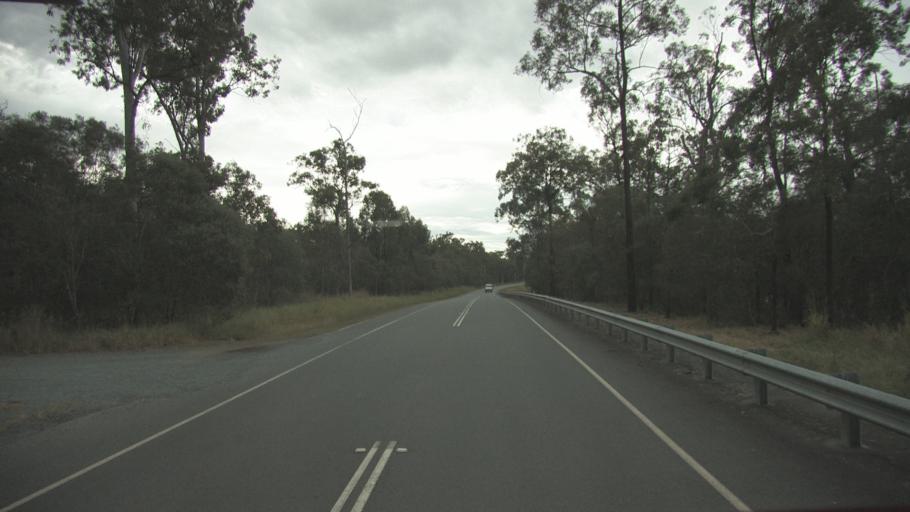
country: AU
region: Queensland
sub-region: Logan
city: Park Ridge South
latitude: -27.7423
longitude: 153.0258
